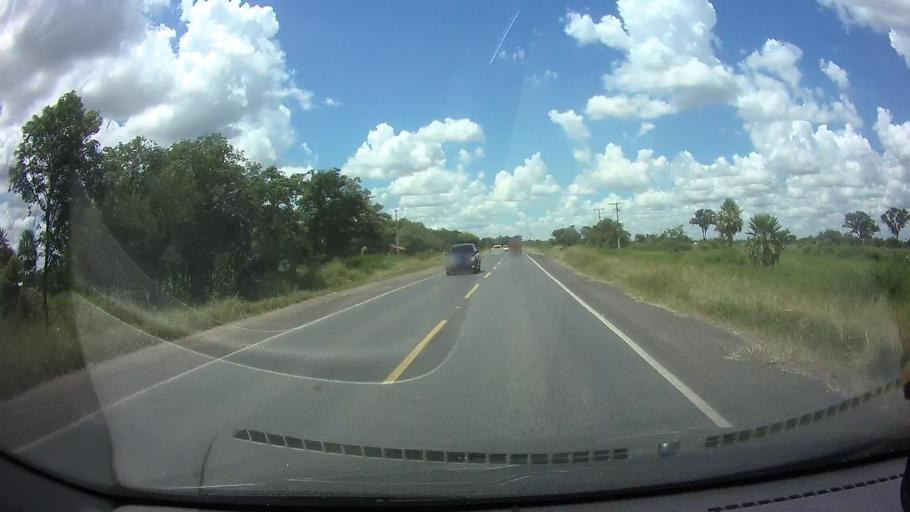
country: PY
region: Presidente Hayes
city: Nanawa
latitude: -25.1950
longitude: -57.6322
